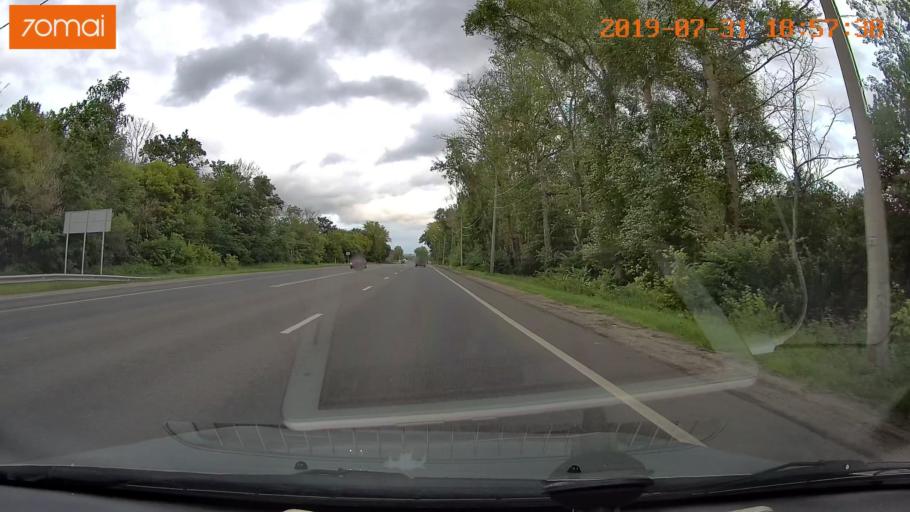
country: RU
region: Moskovskaya
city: Raduzhnyy
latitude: 55.1526
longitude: 38.6947
